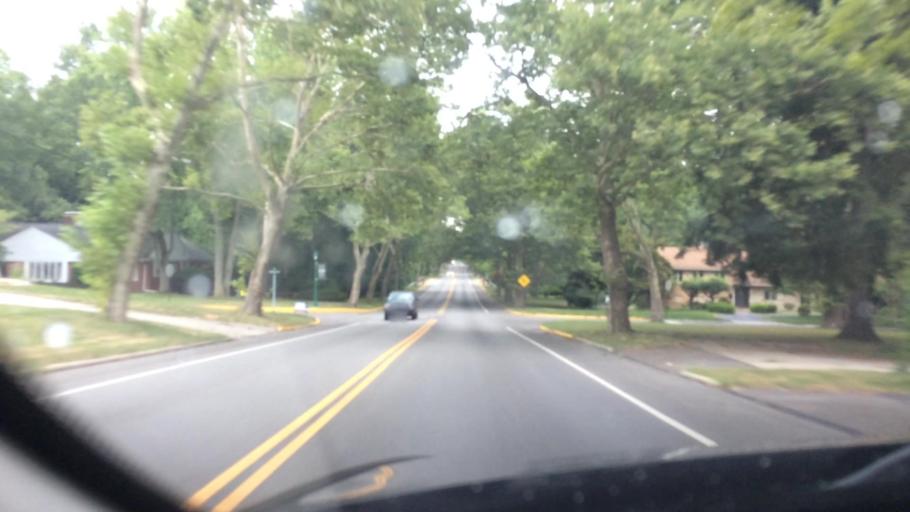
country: US
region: Ohio
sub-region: Lucas County
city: Ottawa Hills
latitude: 41.6638
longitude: -83.6435
